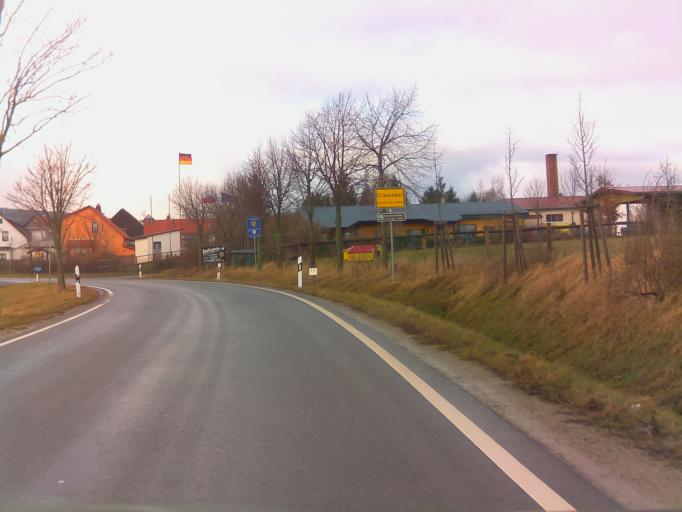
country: DE
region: Thuringia
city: Crawinkel
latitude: 50.7822
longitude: 10.7969
